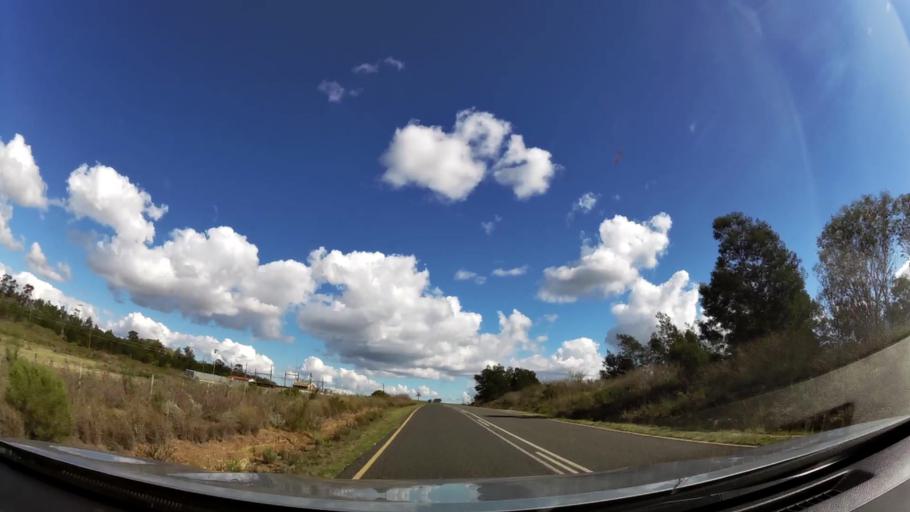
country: ZA
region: Western Cape
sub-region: Overberg District Municipality
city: Swellendam
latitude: -34.0245
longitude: 20.4281
